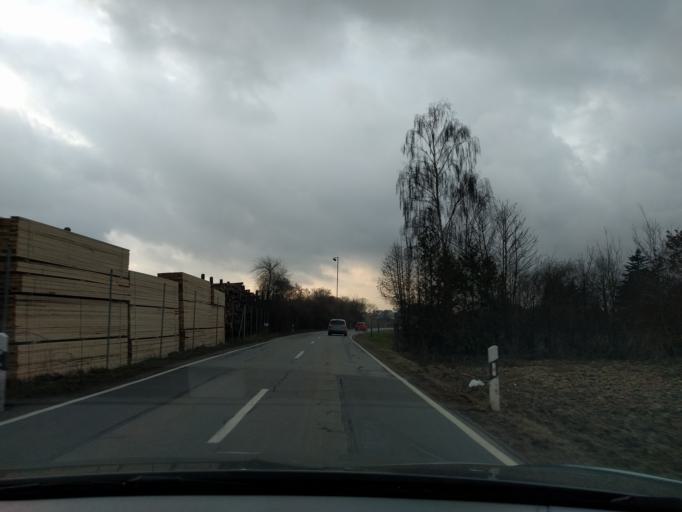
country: DE
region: Bavaria
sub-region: Lower Bavaria
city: Hengersberg
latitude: 48.7669
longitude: 13.0665
